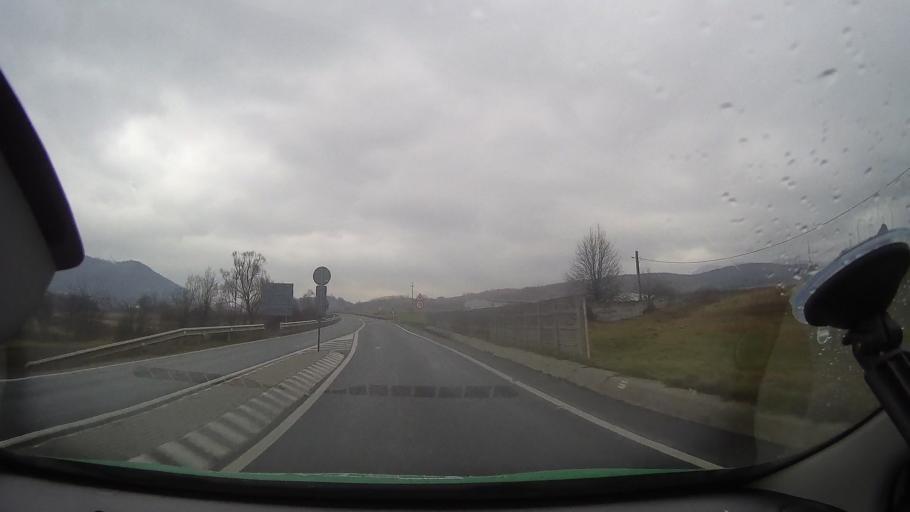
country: RO
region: Hunedoara
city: Vata de Jos
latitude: 46.1875
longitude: 22.6240
